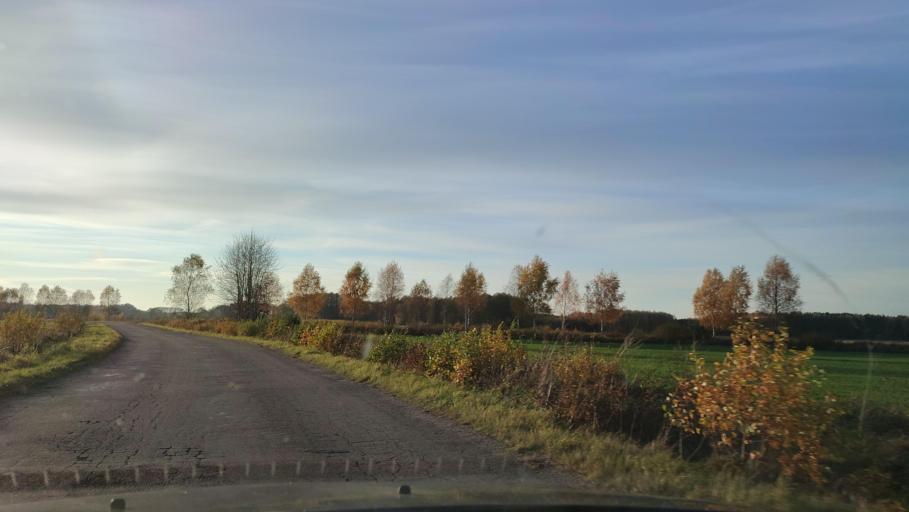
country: PL
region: Masovian Voivodeship
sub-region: Powiat mlawski
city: Dzierzgowo
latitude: 53.3326
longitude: 20.7115
